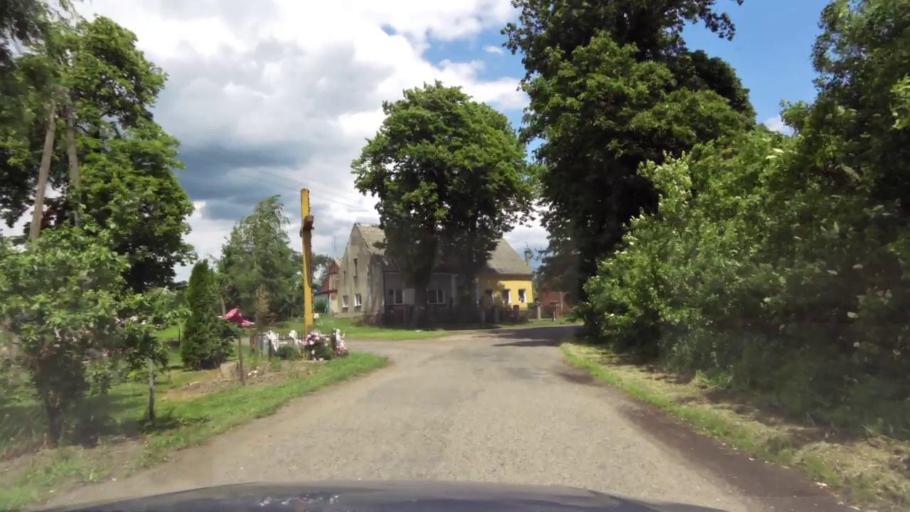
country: PL
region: West Pomeranian Voivodeship
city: Trzcinsko Zdroj
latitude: 52.9451
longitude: 14.7183
